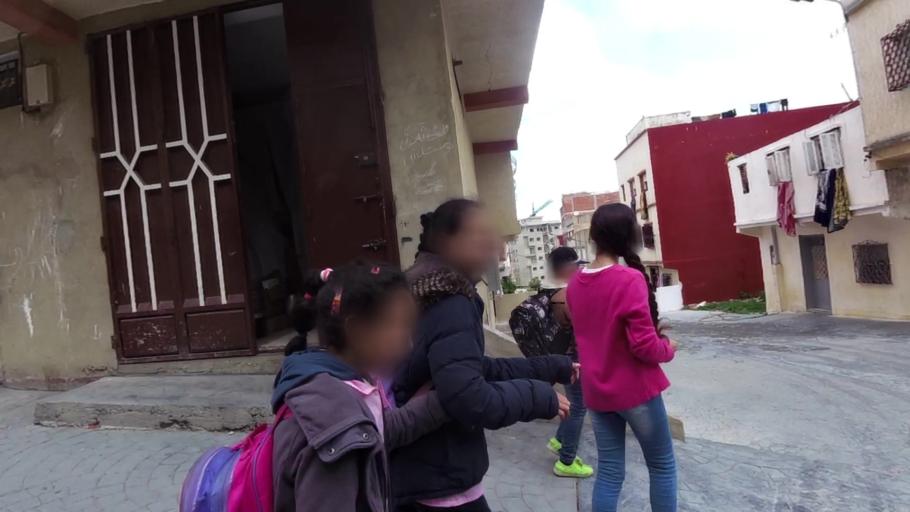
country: MA
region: Tanger-Tetouan
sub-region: Tanger-Assilah
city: Tangier
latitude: 35.7802
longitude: -5.7546
